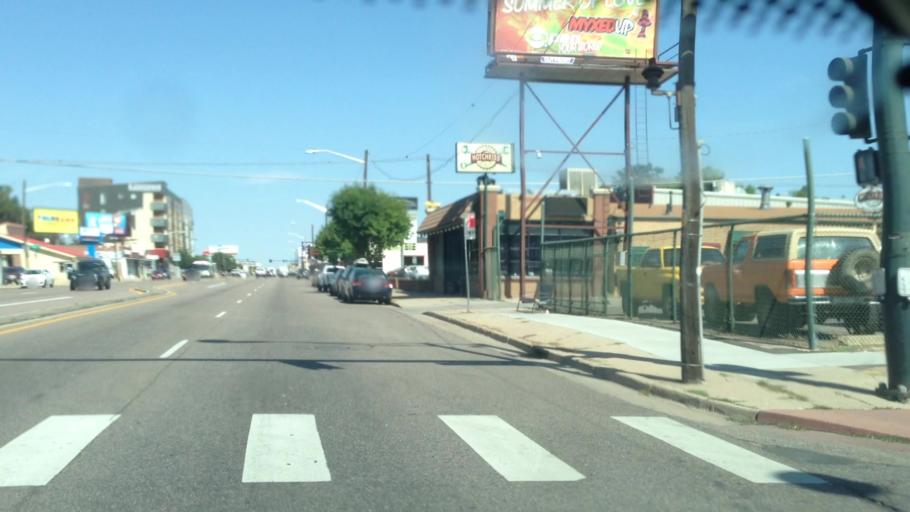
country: US
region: Colorado
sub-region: Arapahoe County
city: Glendale
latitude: 39.7401
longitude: -104.9076
